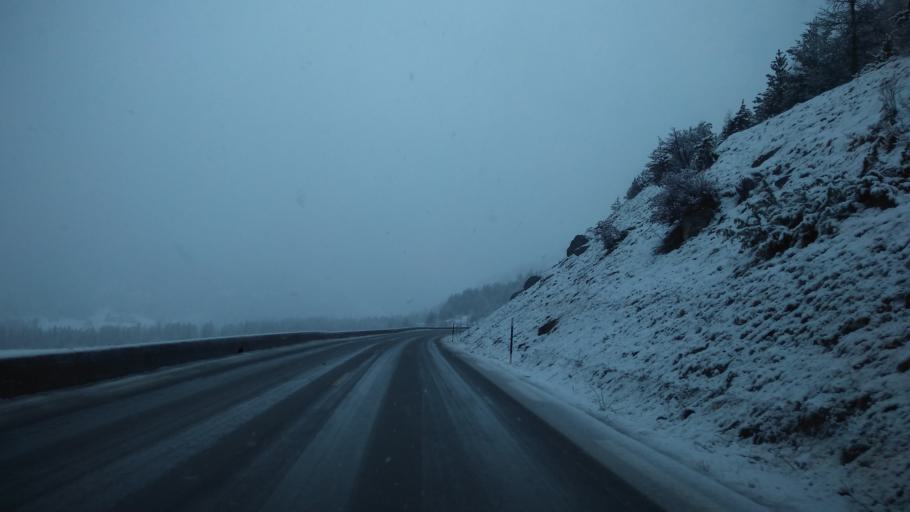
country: FR
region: Provence-Alpes-Cote d'Azur
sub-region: Departement des Hautes-Alpes
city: Le Monetier-les-Bains
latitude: 44.9846
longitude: 6.4963
